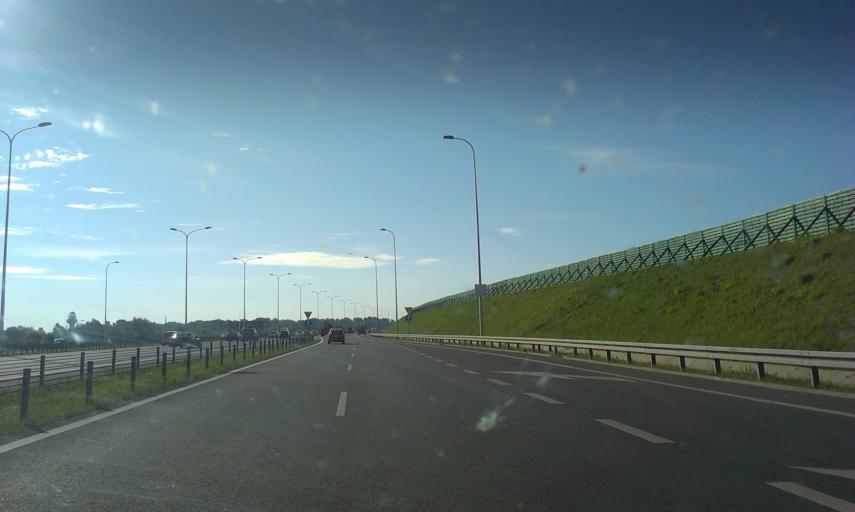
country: PL
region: Masovian Voivodeship
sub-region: Powiat pruszkowski
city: Rybie
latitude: 52.1640
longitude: 20.9418
